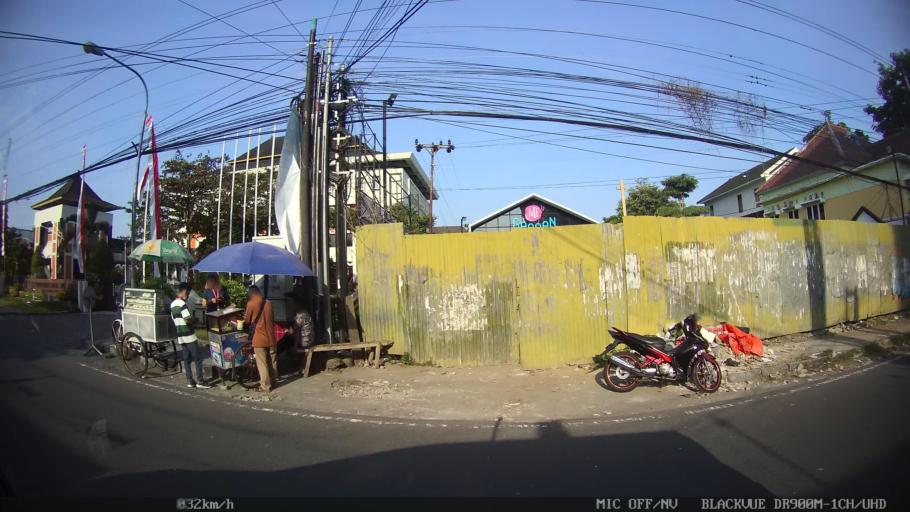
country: ID
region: Daerah Istimewa Yogyakarta
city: Depok
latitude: -7.7796
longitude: 110.4147
